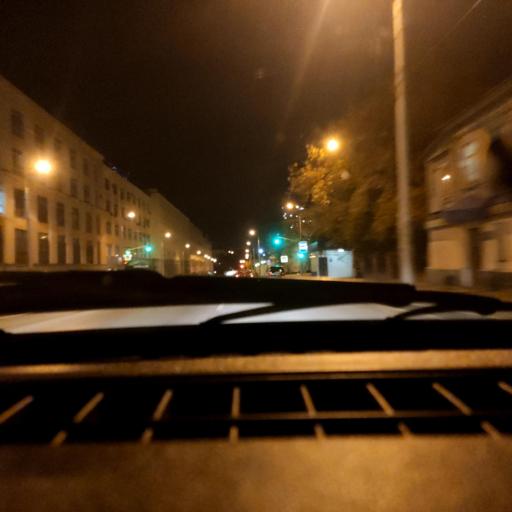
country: RU
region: Bashkortostan
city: Ufa
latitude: 54.7345
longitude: 55.9387
